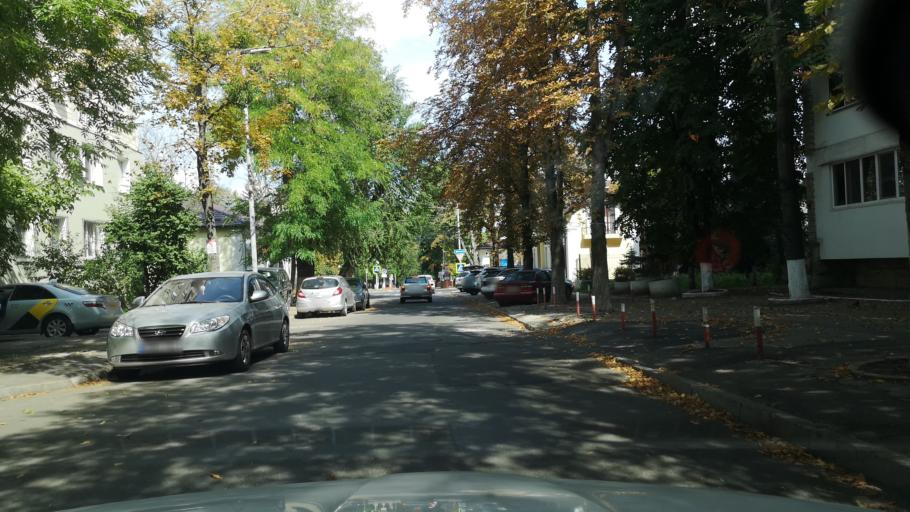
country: MD
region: Chisinau
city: Chisinau
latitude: 47.0221
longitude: 28.8232
